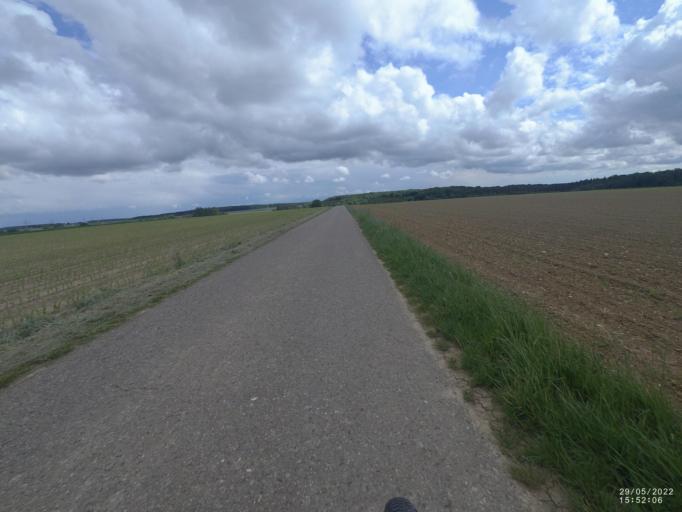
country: DE
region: Baden-Wuerttemberg
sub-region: Tuebingen Region
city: Setzingen
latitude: 48.5779
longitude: 10.1206
